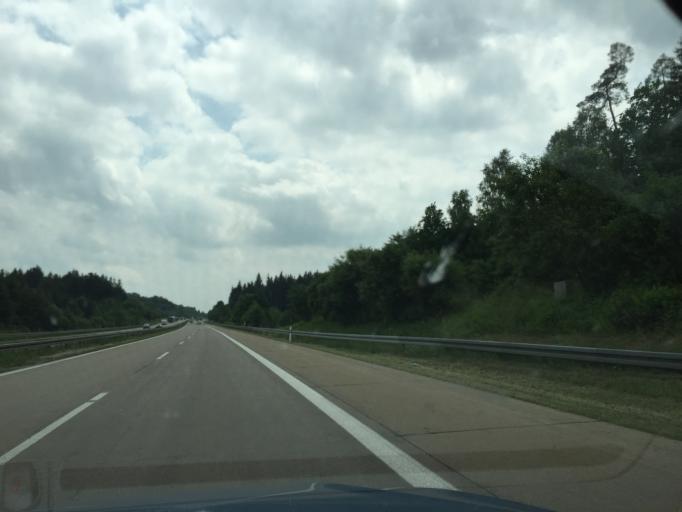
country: DE
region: Baden-Wuerttemberg
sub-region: Regierungsbezirk Stuttgart
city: Ellenberg
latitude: 48.9976
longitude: 10.1938
